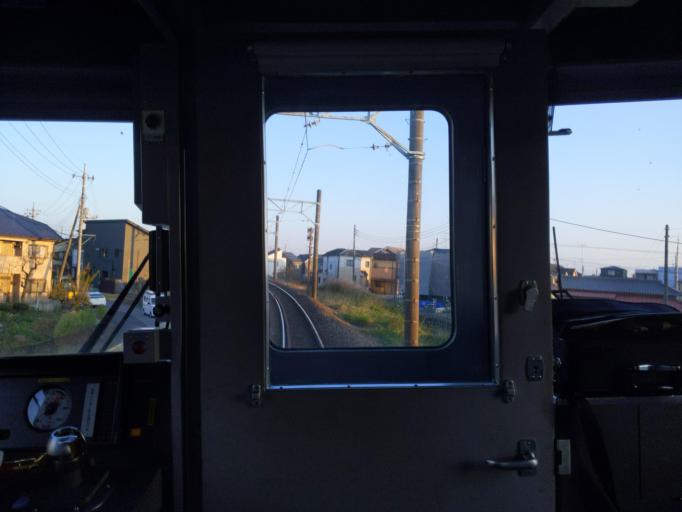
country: JP
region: Saitama
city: Kasukabe
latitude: 35.9756
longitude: 139.7599
